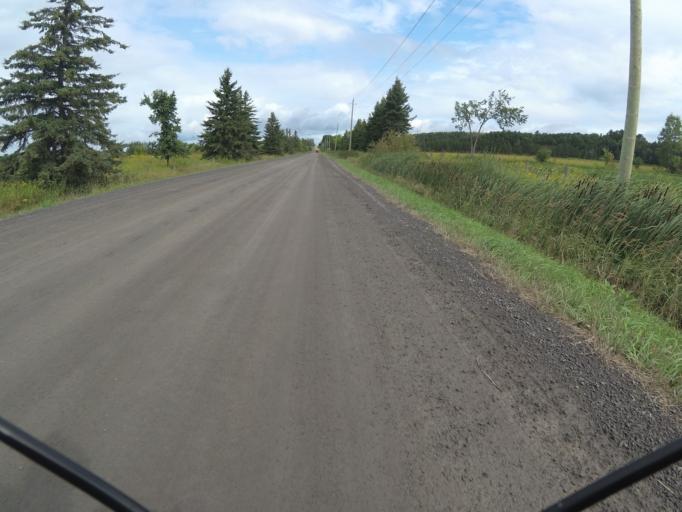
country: CA
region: Ontario
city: Clarence-Rockland
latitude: 45.4805
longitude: -75.3089
